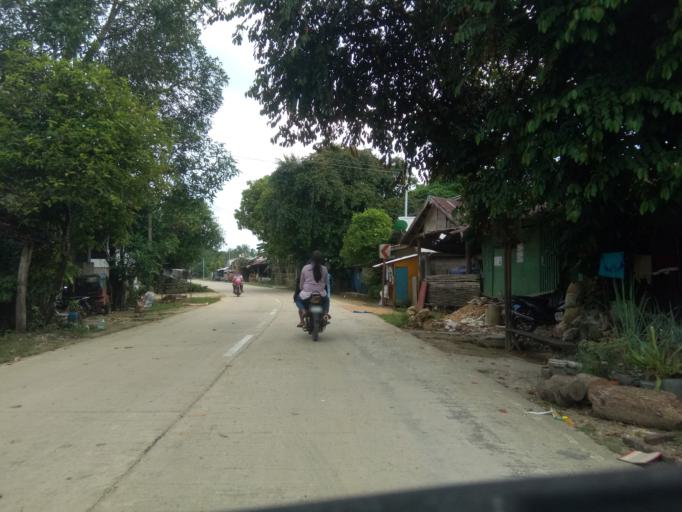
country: PH
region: Caraga
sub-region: Province of Surigao del Norte
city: San Isidro
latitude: 9.9277
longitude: 126.0554
